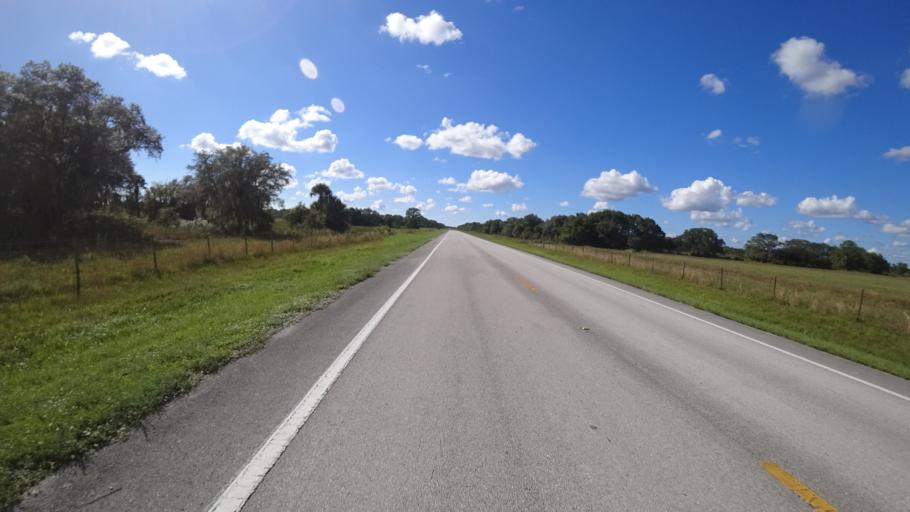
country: US
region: Florida
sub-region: Sarasota County
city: Warm Mineral Springs
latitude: 27.1935
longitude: -82.1764
